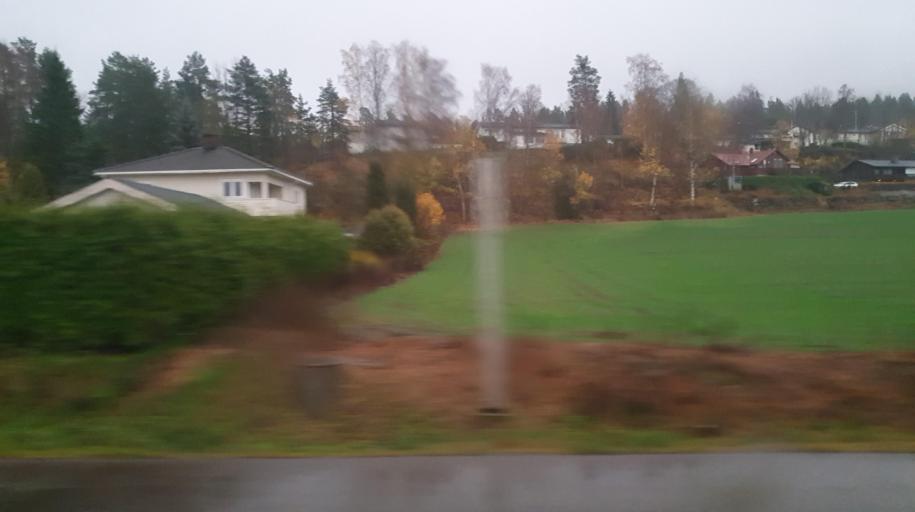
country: NO
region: Buskerud
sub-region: Modum
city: Vikersund
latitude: 59.8899
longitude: 9.9251
